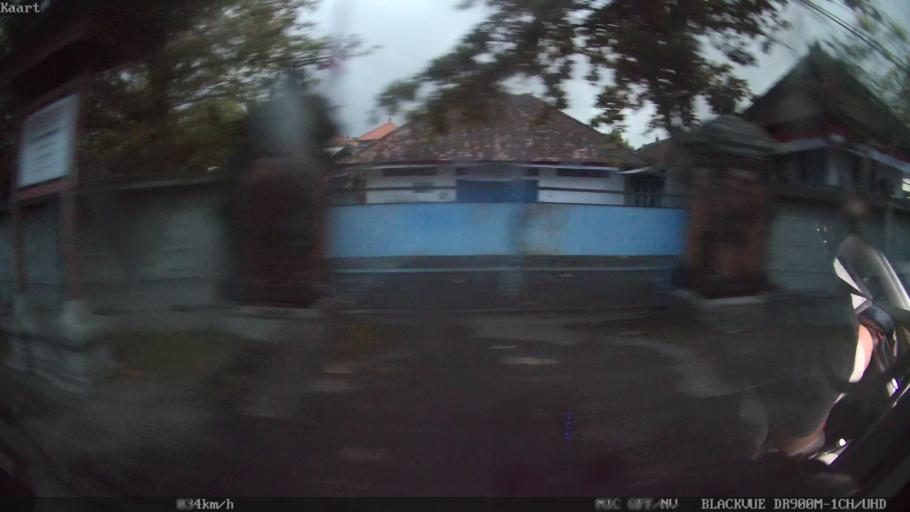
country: ID
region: Bali
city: Banjar Batur
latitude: -8.6011
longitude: 115.2196
